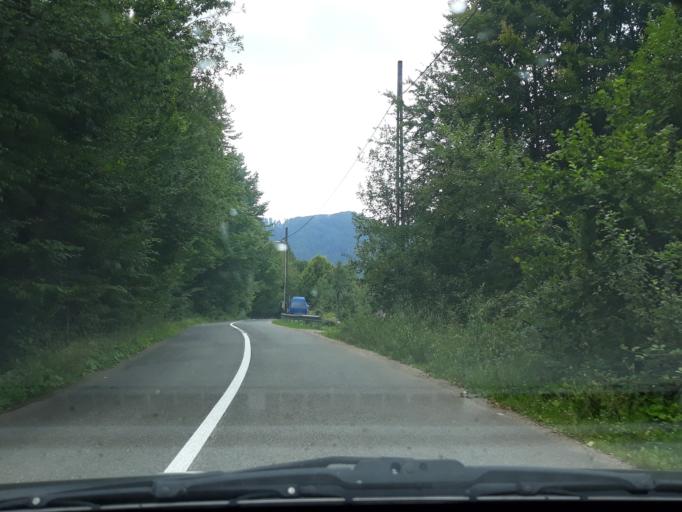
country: RO
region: Bihor
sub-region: Comuna Pietroasa
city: Pietroasa
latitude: 46.5986
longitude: 22.6518
